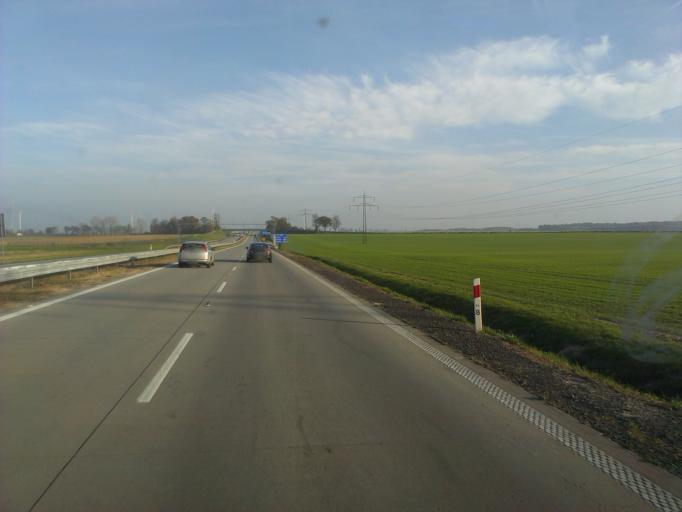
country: PL
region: Lower Silesian Voivodeship
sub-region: Powiat legnicki
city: Legnickie Pole
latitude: 51.1502
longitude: 16.2481
